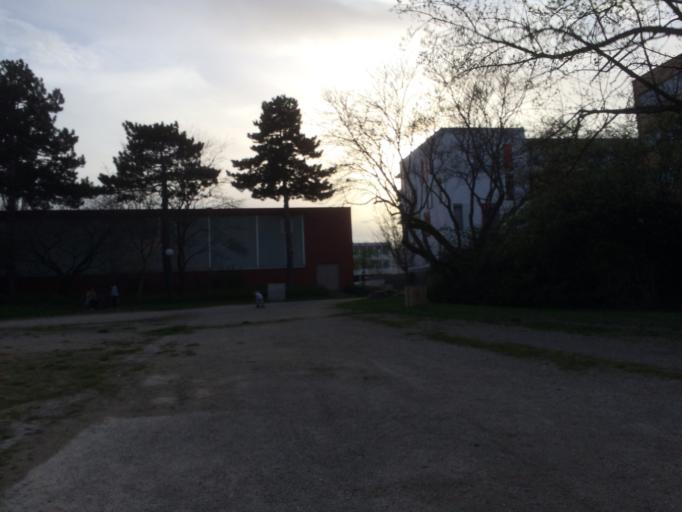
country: FR
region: Ile-de-France
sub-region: Departement des Hauts-de-Seine
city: Antony
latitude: 48.7352
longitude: 2.2993
